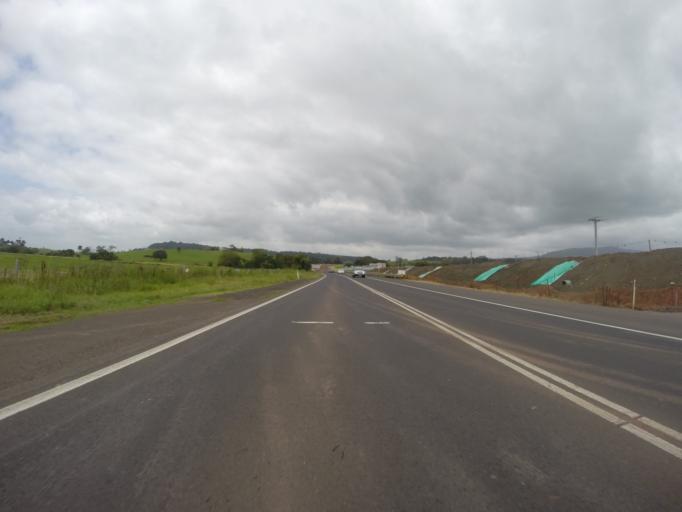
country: AU
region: New South Wales
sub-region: Kiama
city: Gerringong
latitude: -34.7497
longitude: 150.7913
